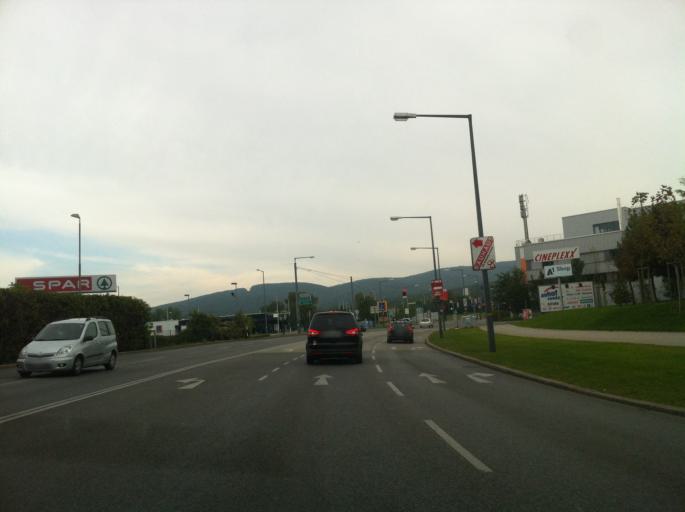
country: AT
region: Lower Austria
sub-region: Politischer Bezirk Wien-Umgebung
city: Purkersdorf
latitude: 48.2090
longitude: 16.2145
